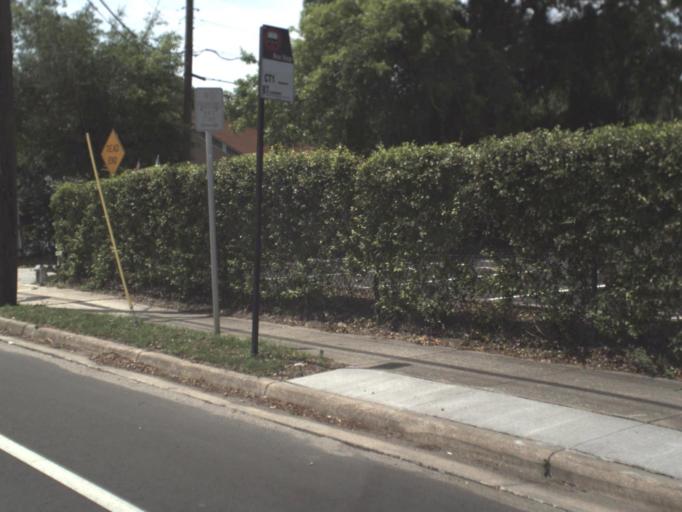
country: US
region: Florida
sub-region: Duval County
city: Jacksonville
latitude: 30.2415
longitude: -81.6251
